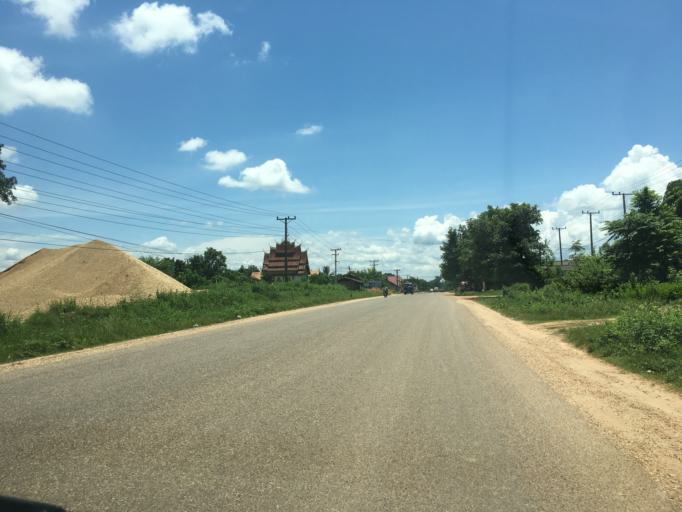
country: LA
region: Vientiane
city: Muang Phon-Hong
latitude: 18.2572
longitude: 102.4873
